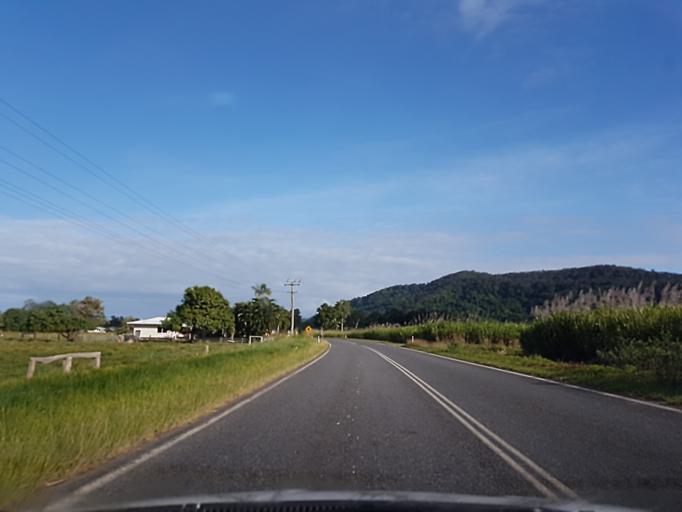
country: AU
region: Queensland
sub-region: Cairns
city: Port Douglas
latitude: -16.3431
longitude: 145.4090
